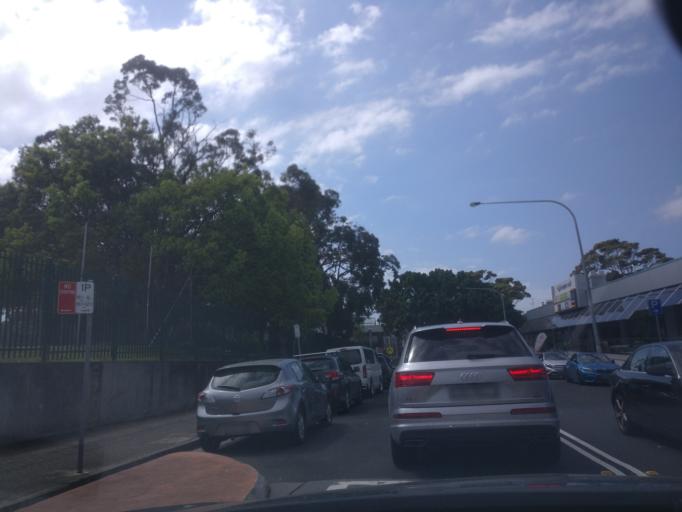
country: AU
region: New South Wales
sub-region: Pittwater
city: Warriewood
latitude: -33.6778
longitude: 151.3016
